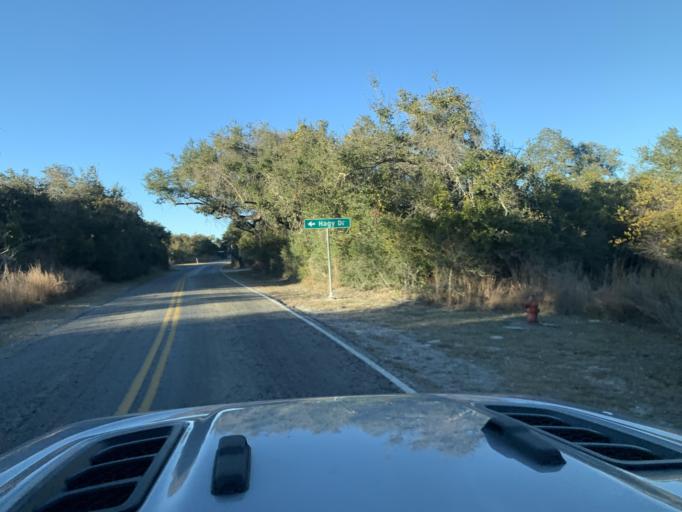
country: US
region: Texas
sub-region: Aransas County
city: Fulton
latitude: 28.1398
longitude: -96.9842
